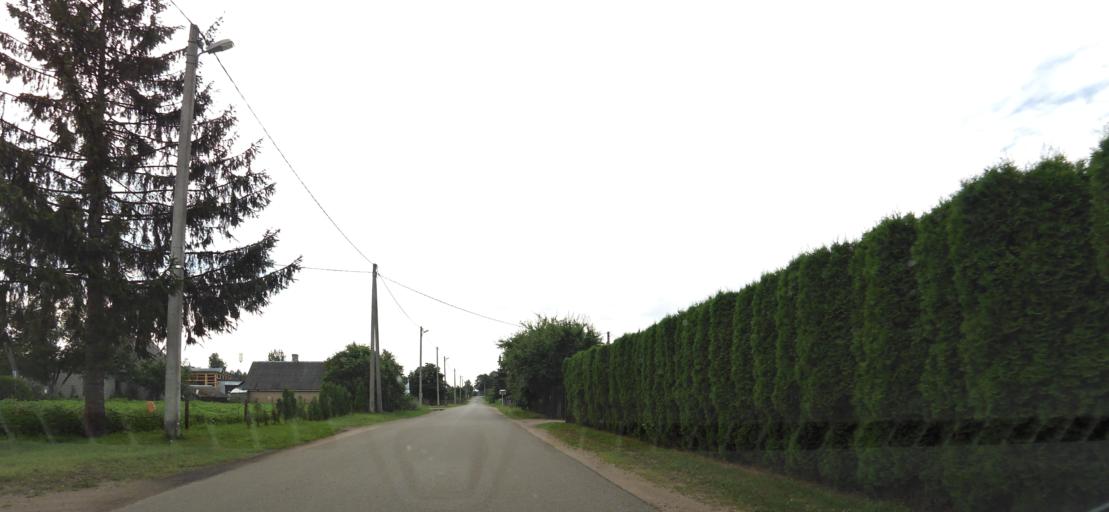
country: LT
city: Trakai
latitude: 54.4983
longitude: 24.9857
